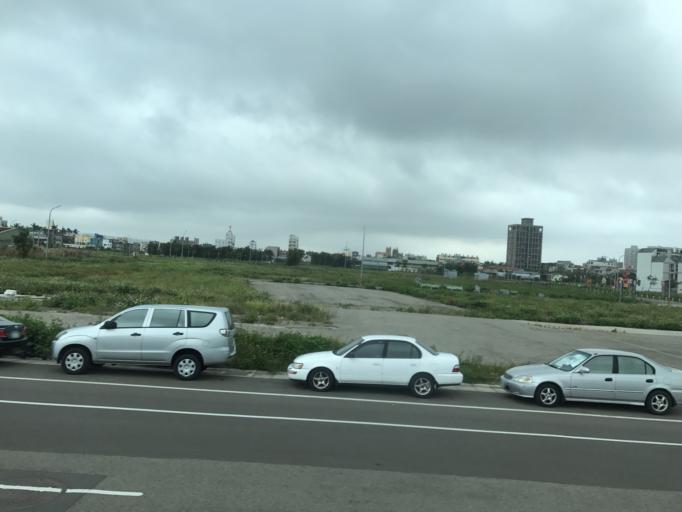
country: TW
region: Taiwan
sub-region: Hsinchu
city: Hsinchu
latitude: 24.8194
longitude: 120.9541
